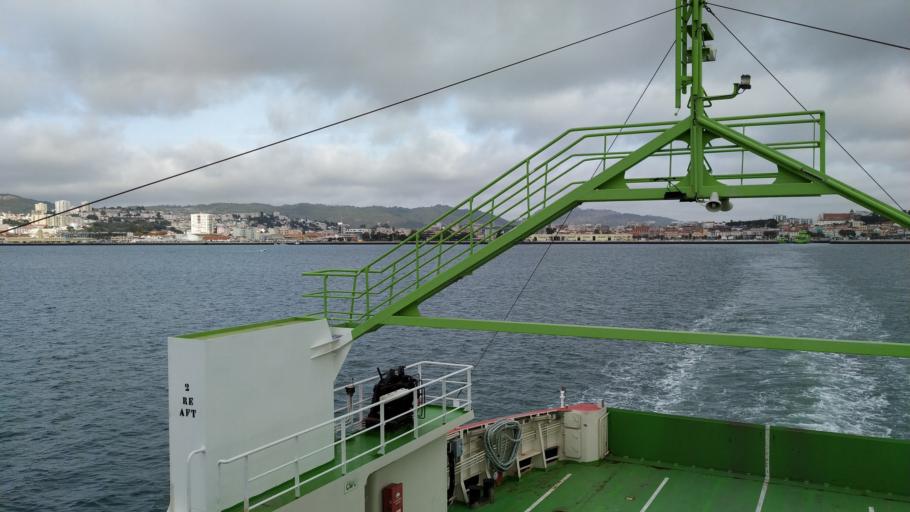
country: PT
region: Setubal
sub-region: Setubal
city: Setubal
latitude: 38.5121
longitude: -8.8866
